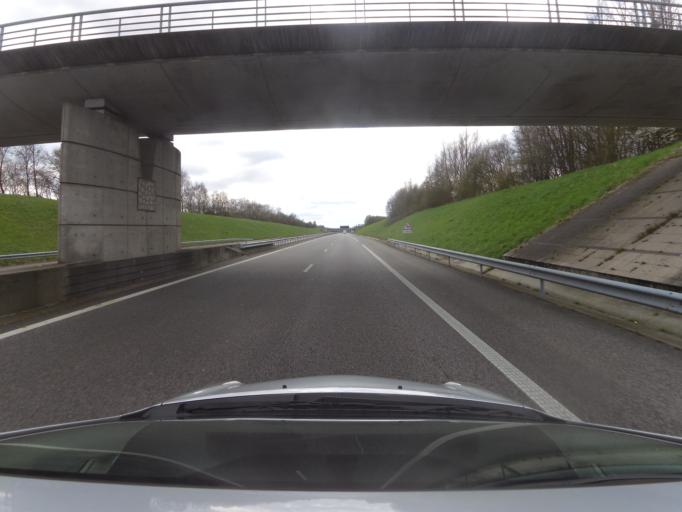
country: FR
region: Haute-Normandie
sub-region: Departement de la Seine-Maritime
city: Saint-Aubin-Routot
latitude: 49.5242
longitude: 0.3070
